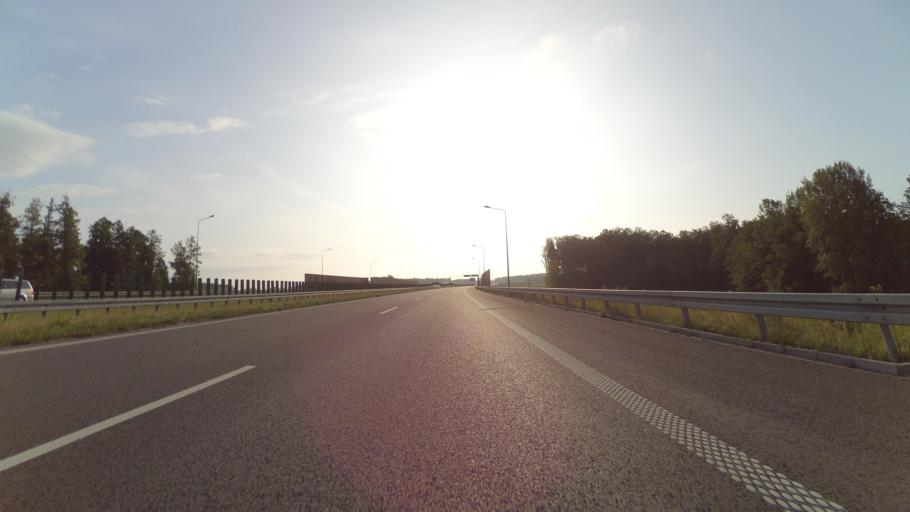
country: PL
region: Podlasie
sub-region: Powiat wysokomazowiecki
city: Sokoly
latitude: 53.1160
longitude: 22.6095
